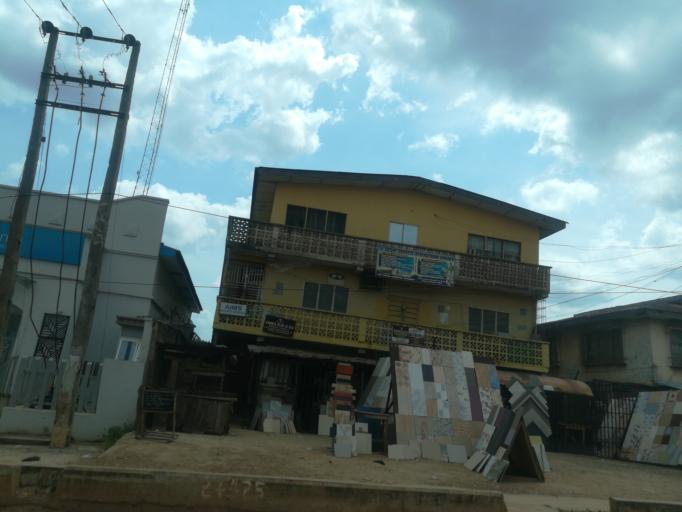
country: NG
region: Oyo
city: Ibadan
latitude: 7.4034
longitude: 3.9357
